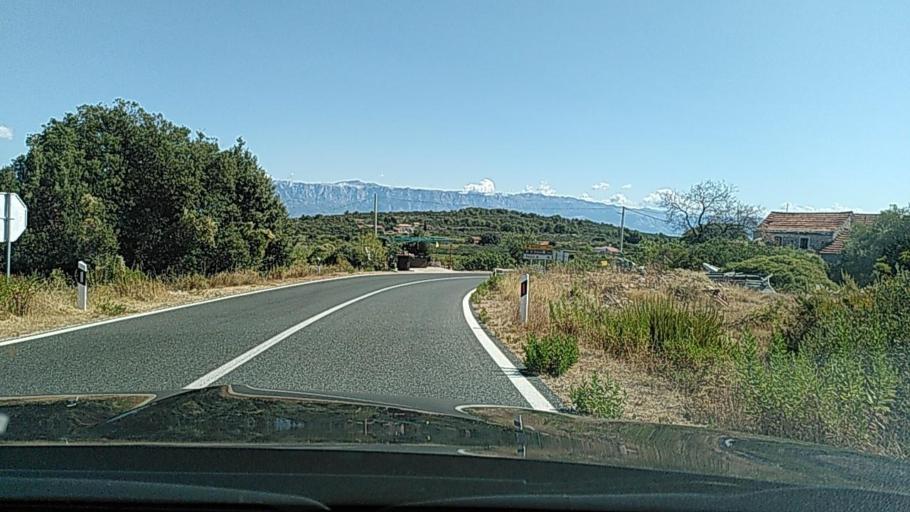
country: HR
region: Splitsko-Dalmatinska
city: Jelsa
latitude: 43.1487
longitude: 16.7896
